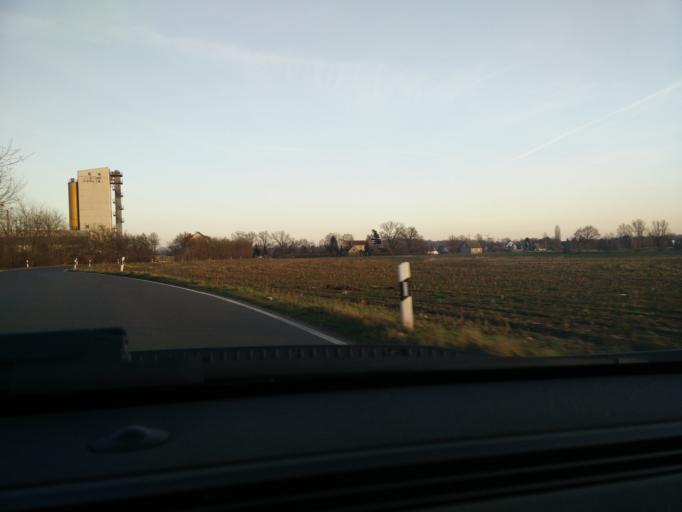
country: DE
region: Saxony
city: Bad Lausick
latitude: 51.1480
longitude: 12.6130
